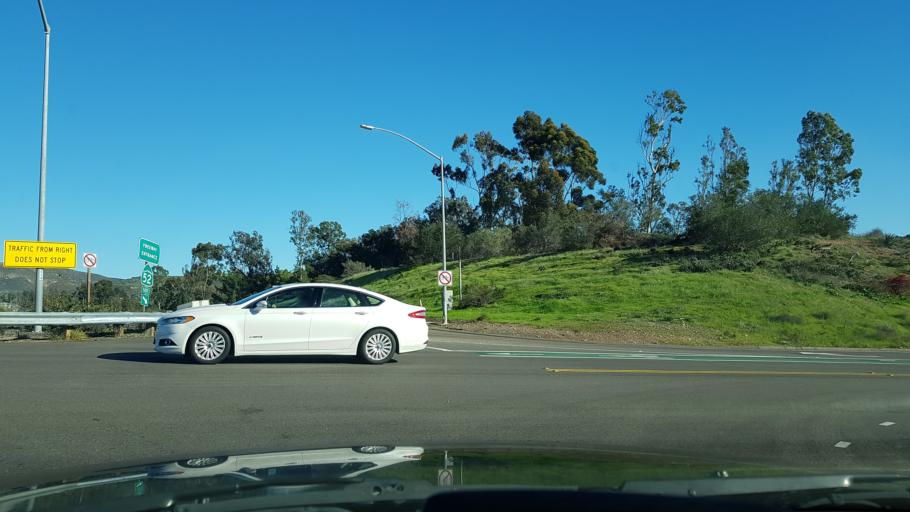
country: US
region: California
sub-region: San Diego County
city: La Mesa
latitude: 32.8408
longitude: -117.0975
